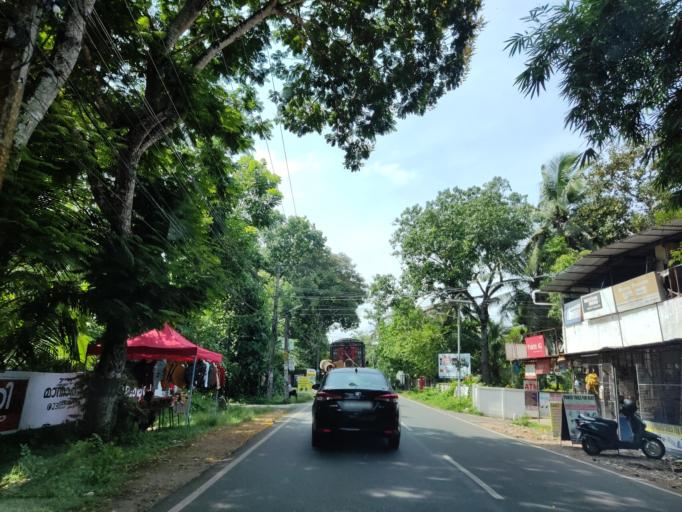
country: IN
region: Kerala
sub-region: Alappuzha
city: Mavelikara
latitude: 9.2948
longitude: 76.5330
